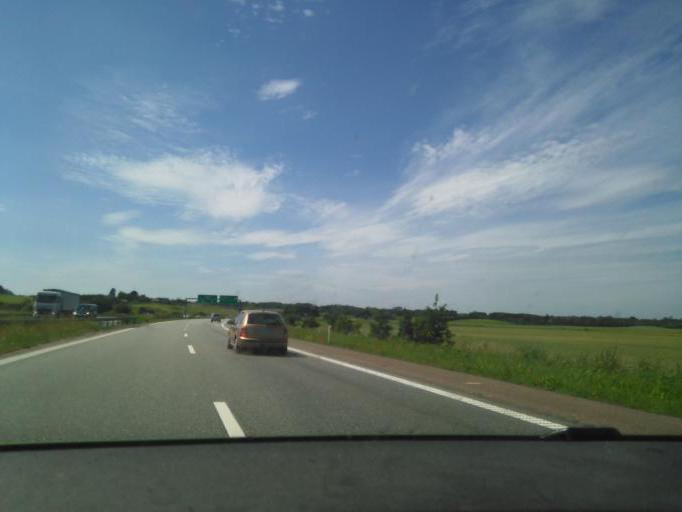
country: DK
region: Zealand
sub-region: Holbaek Kommune
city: Tollose
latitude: 55.6488
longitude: 11.7845
